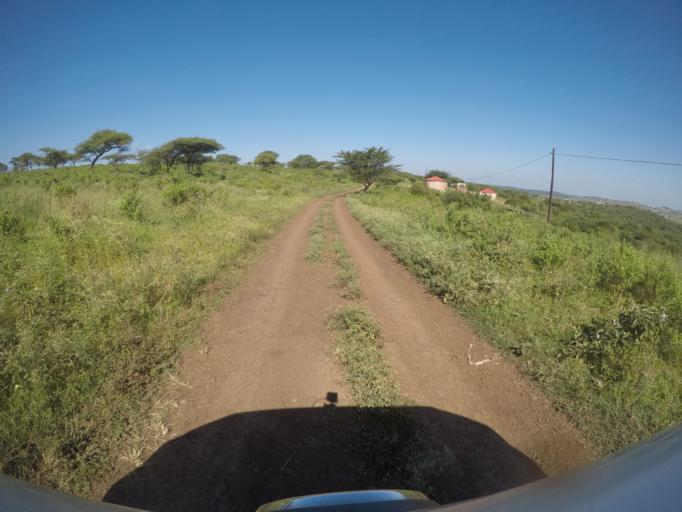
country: ZA
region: KwaZulu-Natal
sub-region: uThungulu District Municipality
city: Empangeni
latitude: -28.5706
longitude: 31.7358
